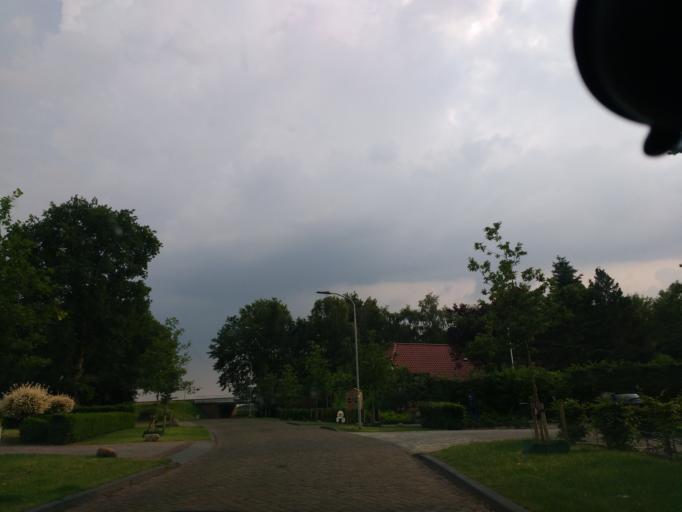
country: NL
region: Drenthe
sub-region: Gemeente Borger-Odoorn
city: Borger
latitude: 52.9069
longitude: 6.8040
